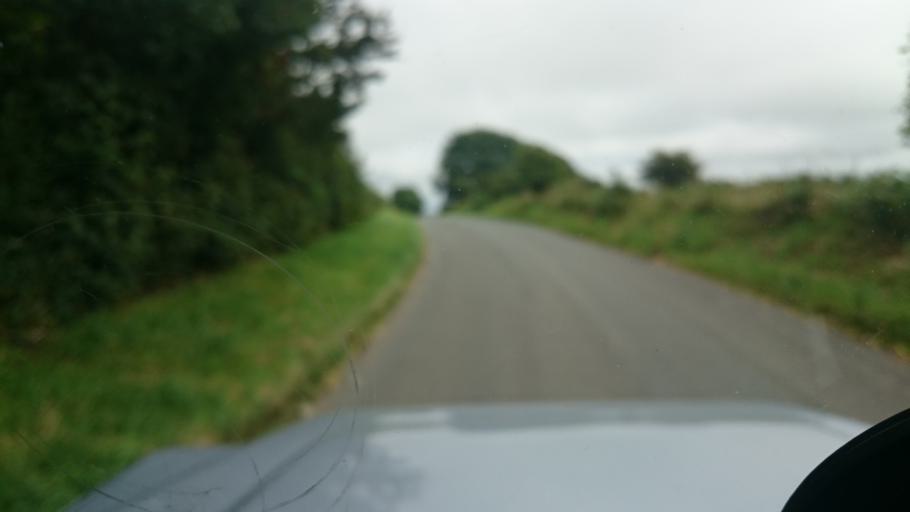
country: GB
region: Wales
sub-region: Pembrokeshire
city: Ambleston
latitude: 51.9257
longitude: -4.9512
